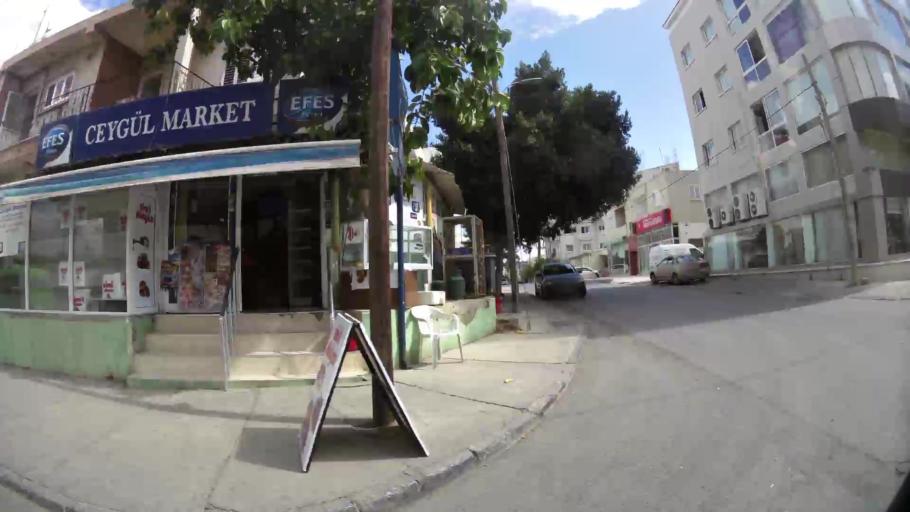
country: CY
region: Lefkosia
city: Nicosia
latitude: 35.1995
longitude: 33.3442
